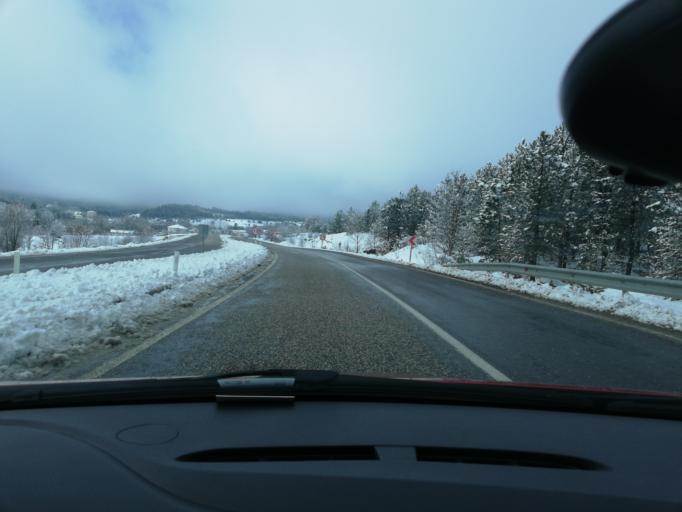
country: TR
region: Kastamonu
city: Ihsangazi
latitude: 41.3049
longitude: 33.5515
